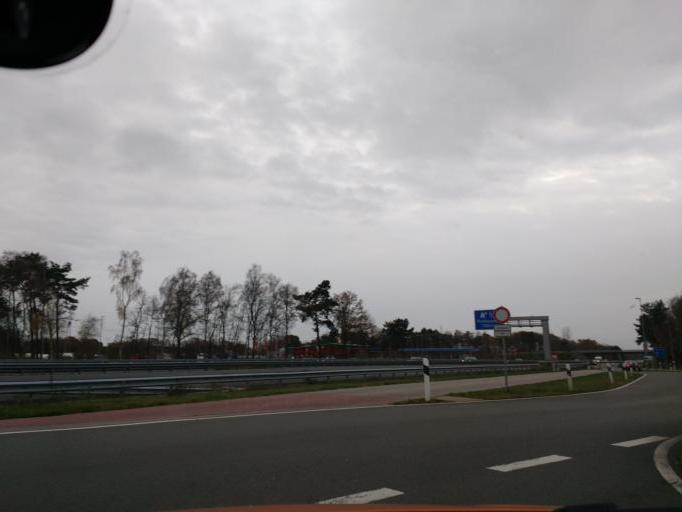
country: DE
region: Lower Saxony
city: Ottersberg
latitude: 53.0896
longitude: 9.1772
